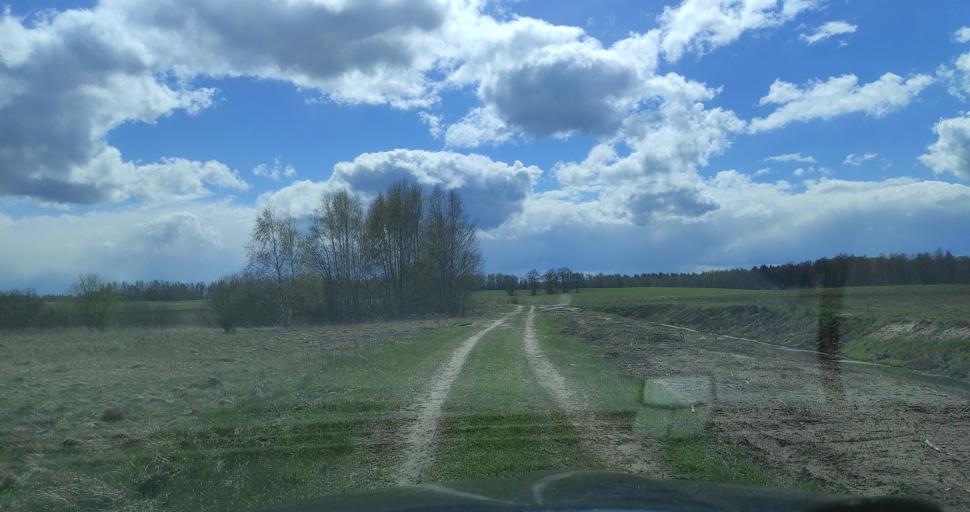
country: LV
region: Kuldigas Rajons
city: Kuldiga
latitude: 56.8734
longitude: 21.7897
